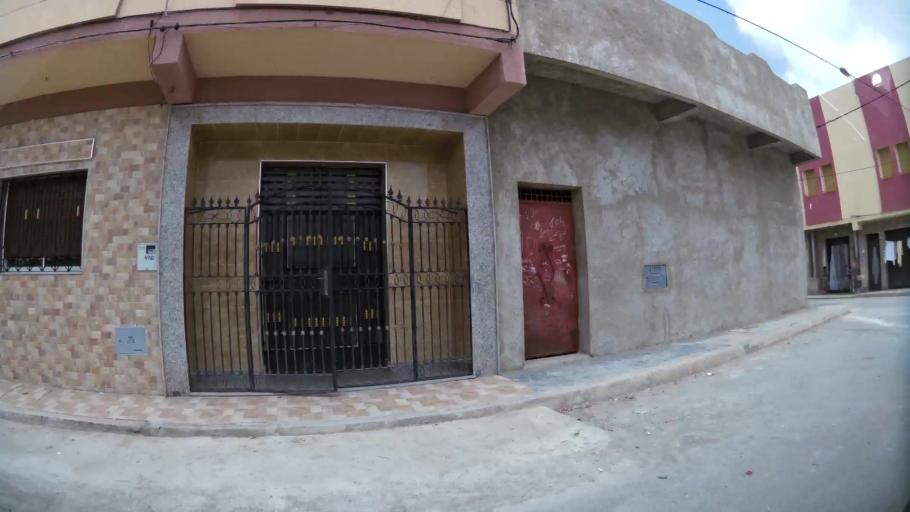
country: MA
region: Oriental
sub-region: Nador
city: Nador
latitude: 35.1702
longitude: -2.9163
